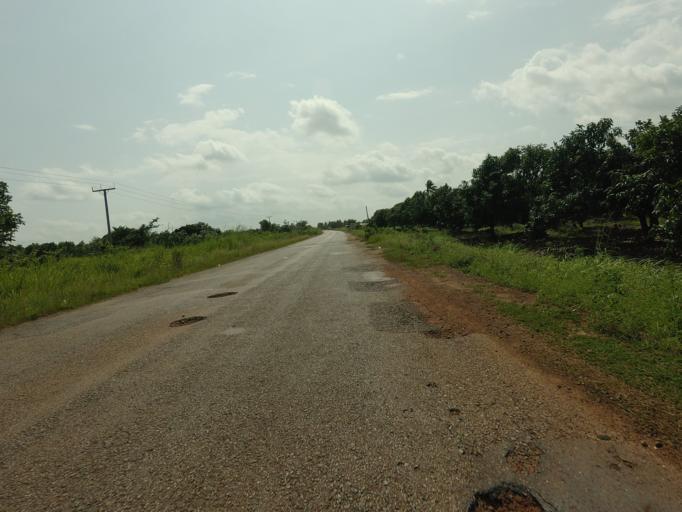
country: TG
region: Maritime
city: Lome
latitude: 6.2539
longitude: 0.9685
